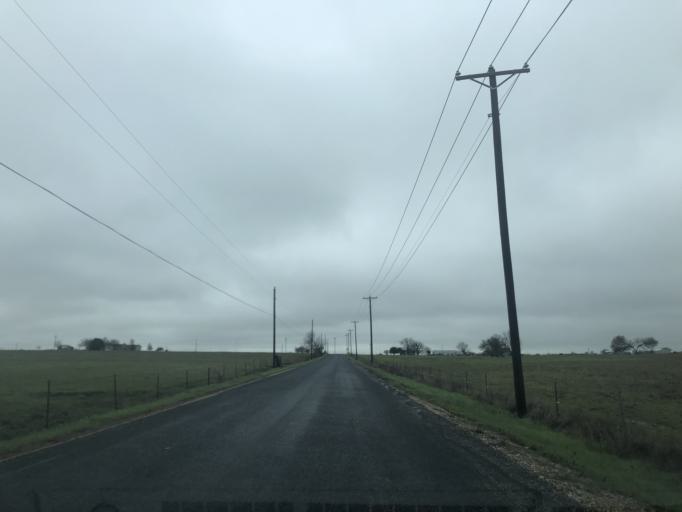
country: US
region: Texas
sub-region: Williamson County
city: Serenada
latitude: 30.7617
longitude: -97.6141
